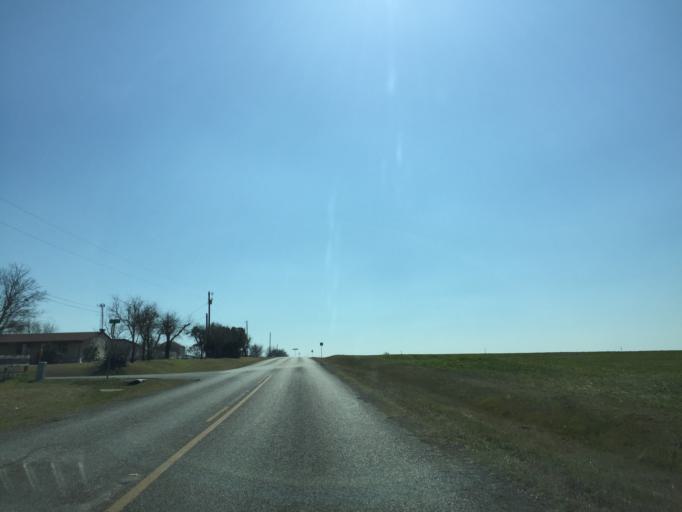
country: US
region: Texas
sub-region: Williamson County
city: Serenada
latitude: 30.6919
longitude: -97.5859
